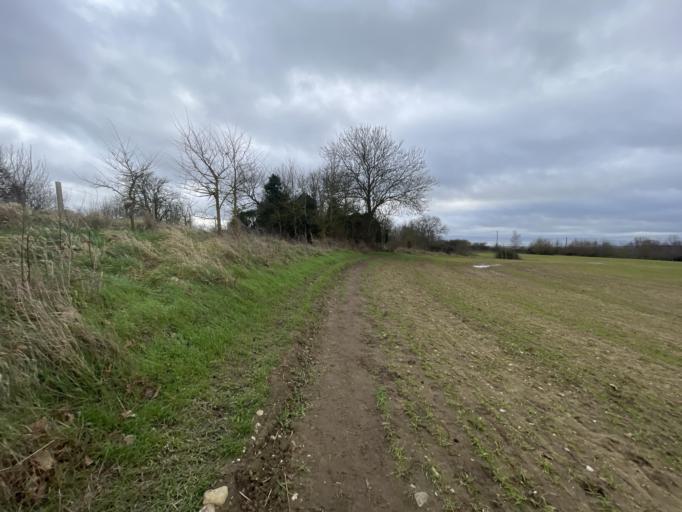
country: GB
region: England
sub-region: West Berkshire
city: Theale
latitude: 51.4453
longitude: -1.0666
